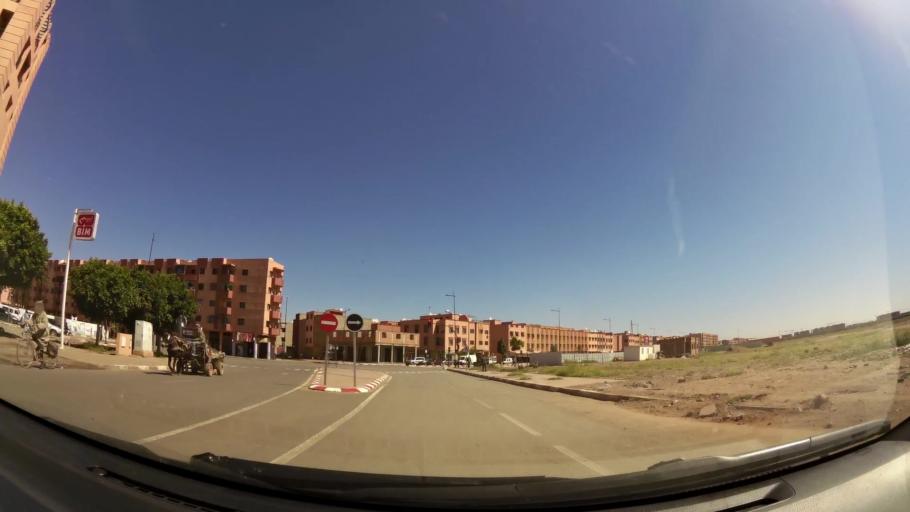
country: MA
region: Marrakech-Tensift-Al Haouz
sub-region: Marrakech
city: Marrakesh
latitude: 31.5807
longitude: -8.0536
